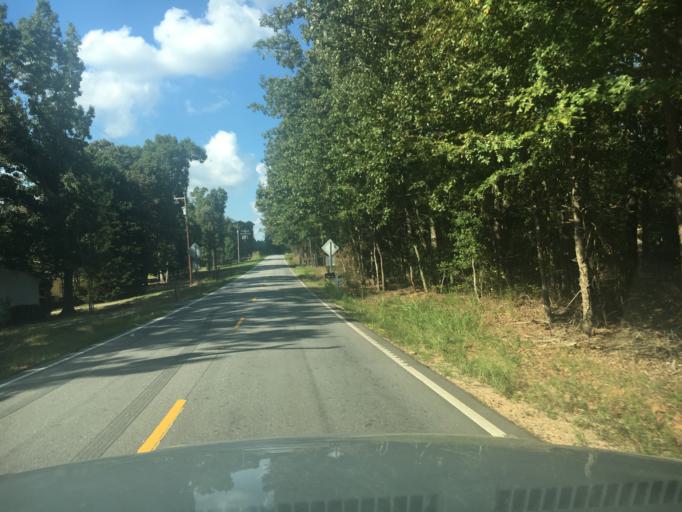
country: US
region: South Carolina
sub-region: Greenville County
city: Fountain Inn
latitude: 34.5640
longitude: -82.2166
